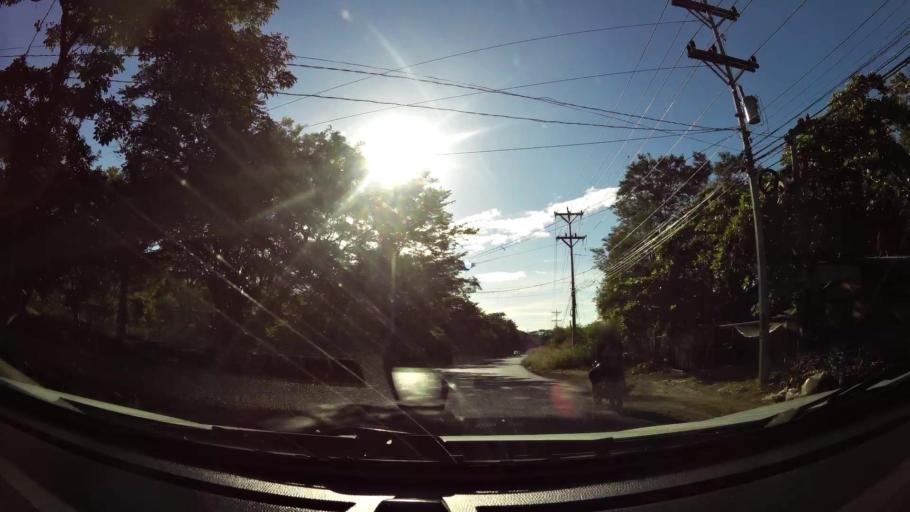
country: CR
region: Guanacaste
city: Sardinal
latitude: 10.5281
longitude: -85.6571
